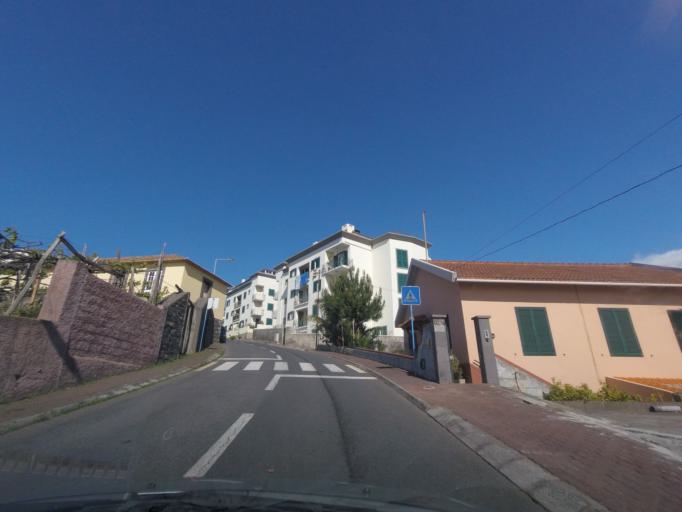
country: PT
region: Madeira
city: Camara de Lobos
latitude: 32.6702
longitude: -16.9759
